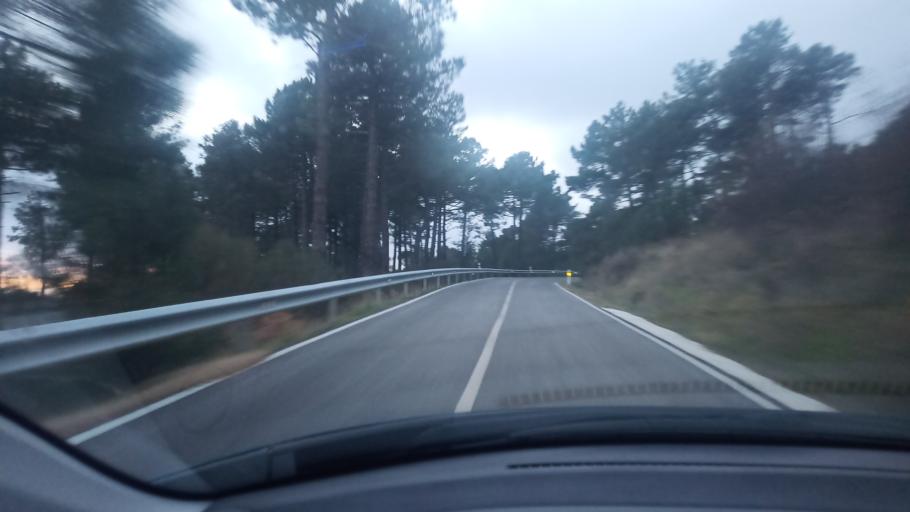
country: ES
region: Madrid
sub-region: Provincia de Madrid
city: Zarzalejo
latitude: 40.5563
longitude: -4.1870
